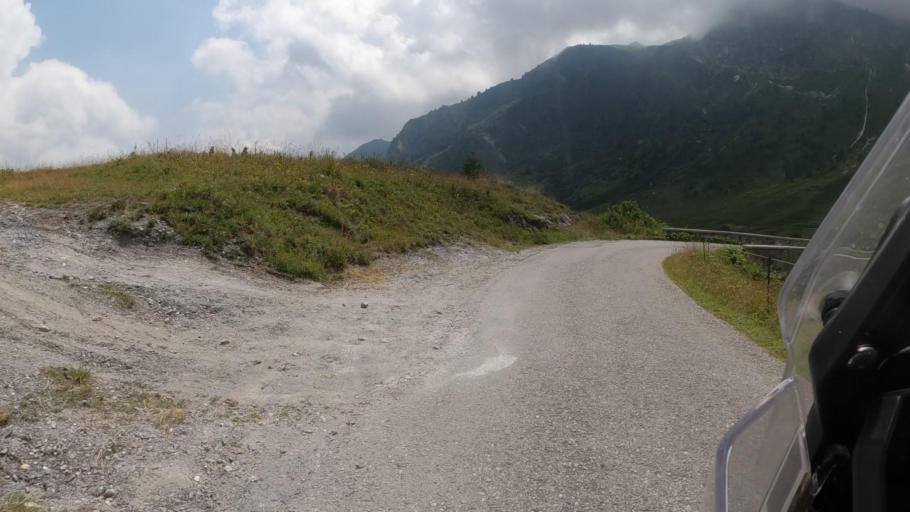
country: IT
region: Piedmont
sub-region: Provincia di Cuneo
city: Campomolino
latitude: 44.3934
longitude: 7.1487
